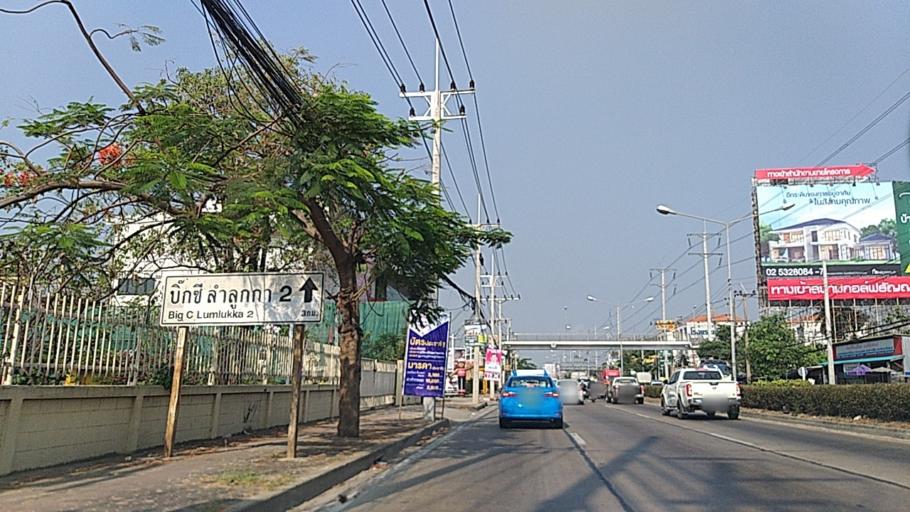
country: TH
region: Pathum Thani
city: Lam Luk Ka
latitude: 13.9332
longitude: 100.6973
